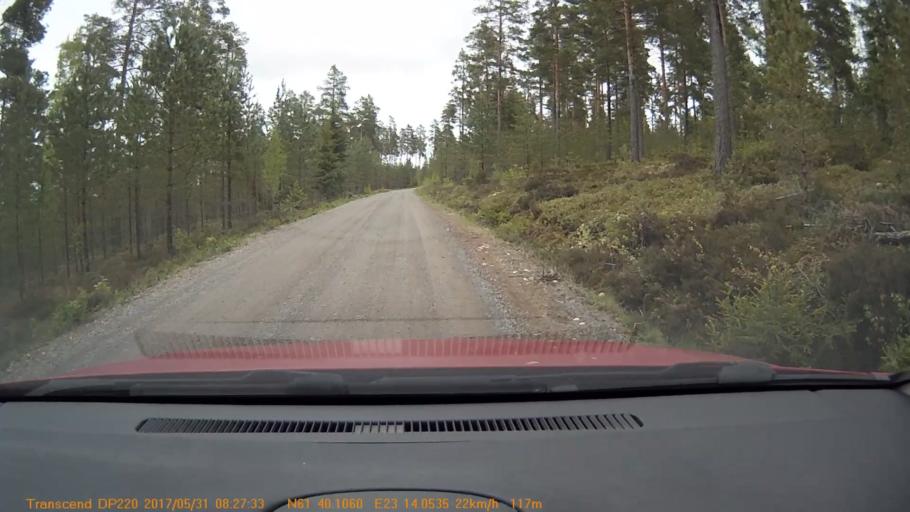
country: FI
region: Pirkanmaa
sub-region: Tampere
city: Haemeenkyroe
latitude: 61.6684
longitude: 23.2341
